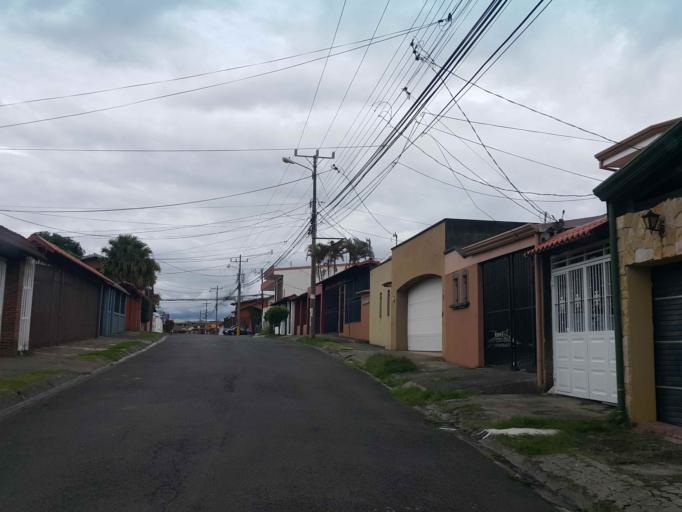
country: CR
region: Heredia
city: Heredia
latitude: 10.0144
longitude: -84.1206
